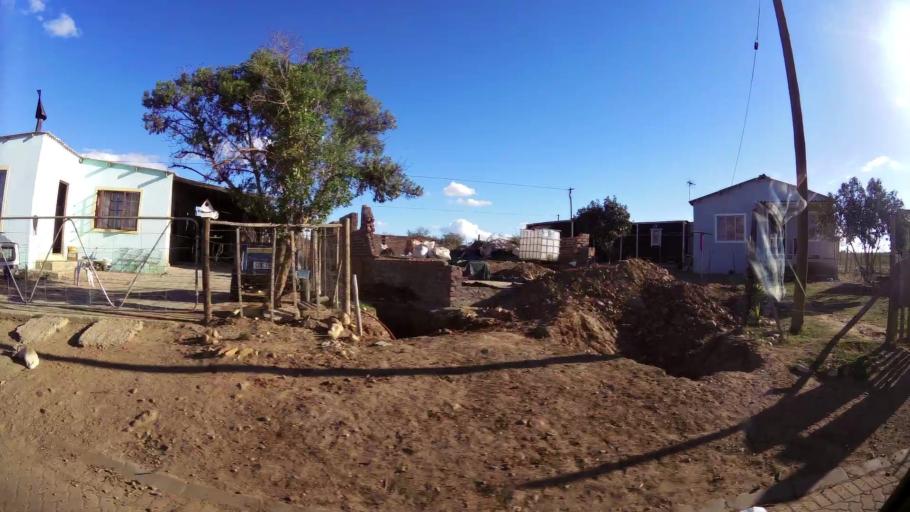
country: ZA
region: Western Cape
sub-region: Eden District Municipality
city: Riversdale
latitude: -34.1082
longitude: 20.9600
